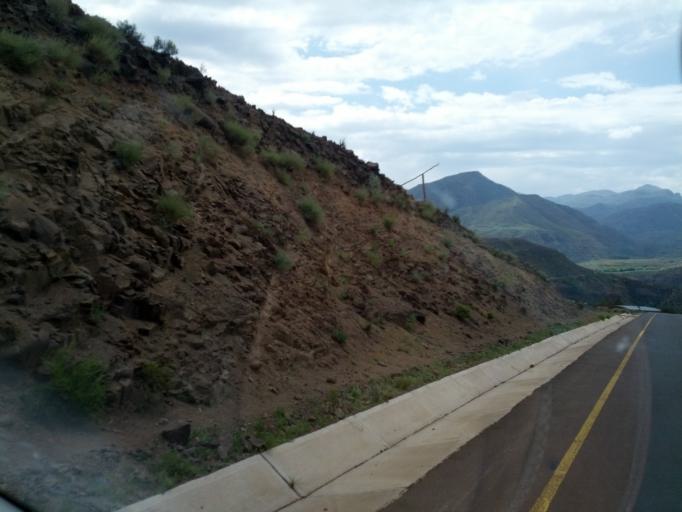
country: LS
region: Maseru
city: Nako
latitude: -29.6599
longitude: 27.7843
